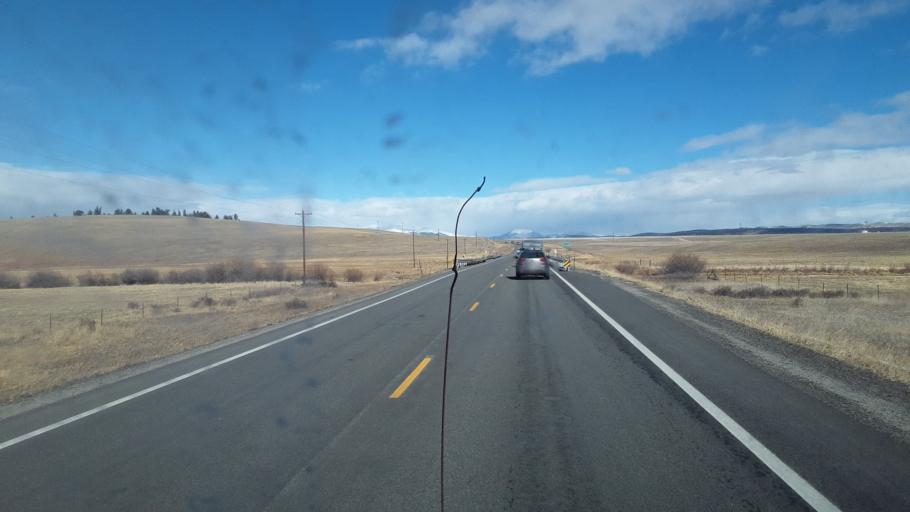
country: US
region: Colorado
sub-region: Park County
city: Fairplay
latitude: 39.0709
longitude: -105.9744
